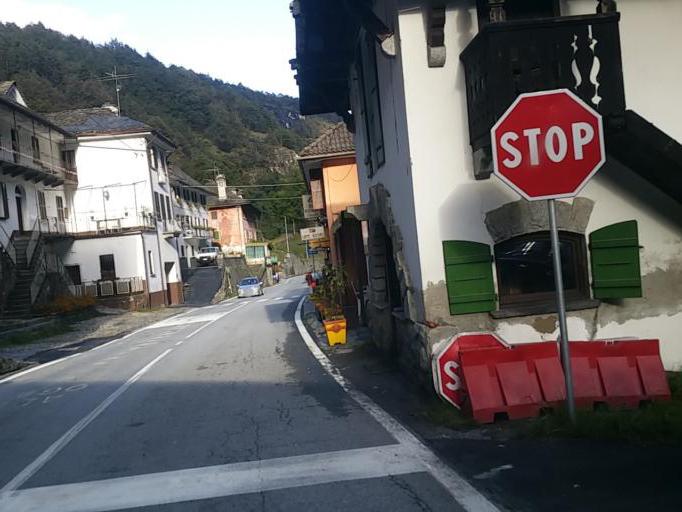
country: IT
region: Piedmont
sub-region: Provincia Verbano-Cusio-Ossola
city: Trasquera
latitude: 46.2052
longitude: 8.1915
